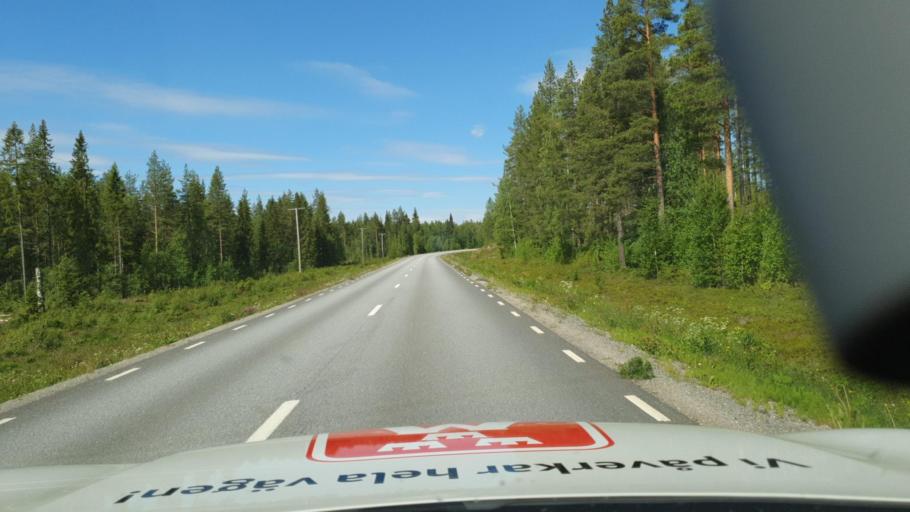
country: SE
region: Vaesterbotten
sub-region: Skelleftea Kommun
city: Boliden
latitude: 64.7457
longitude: 20.3543
